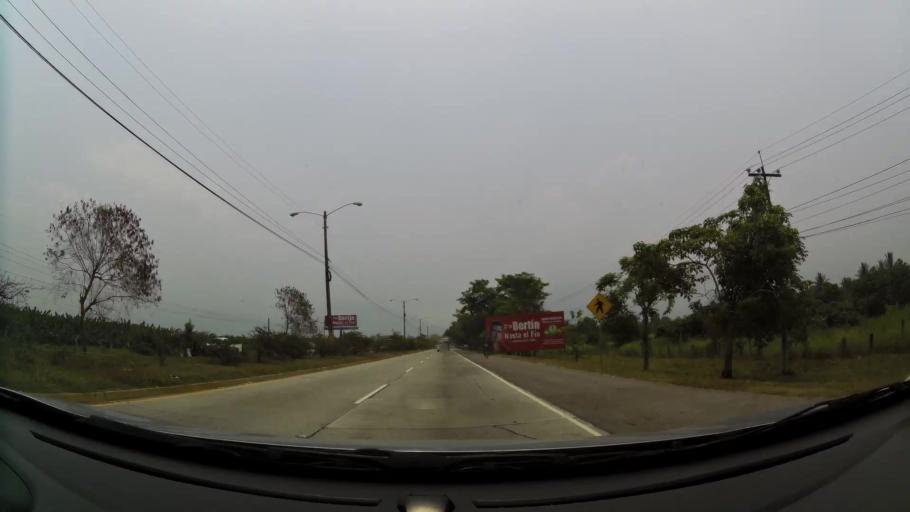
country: HN
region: Yoro
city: El Progreso
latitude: 15.4058
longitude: -87.8263
